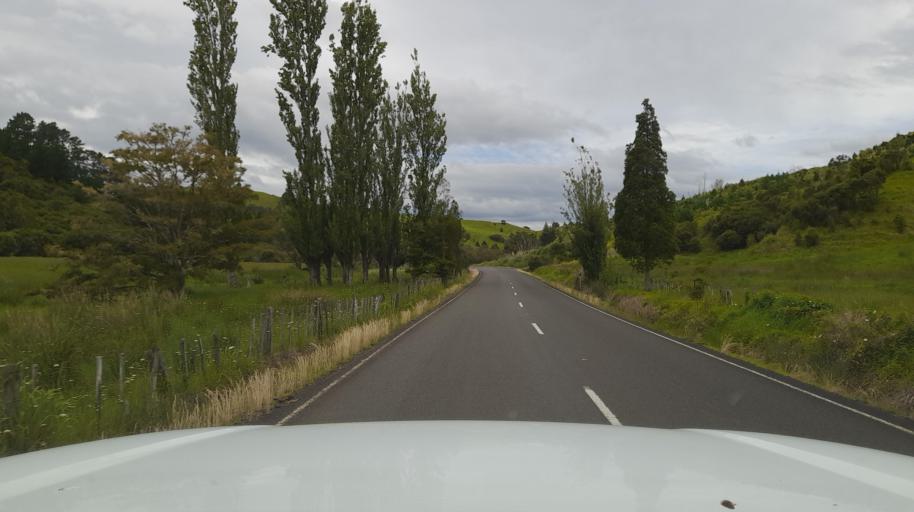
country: NZ
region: Northland
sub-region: Far North District
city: Kaitaia
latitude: -35.3603
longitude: 173.4688
